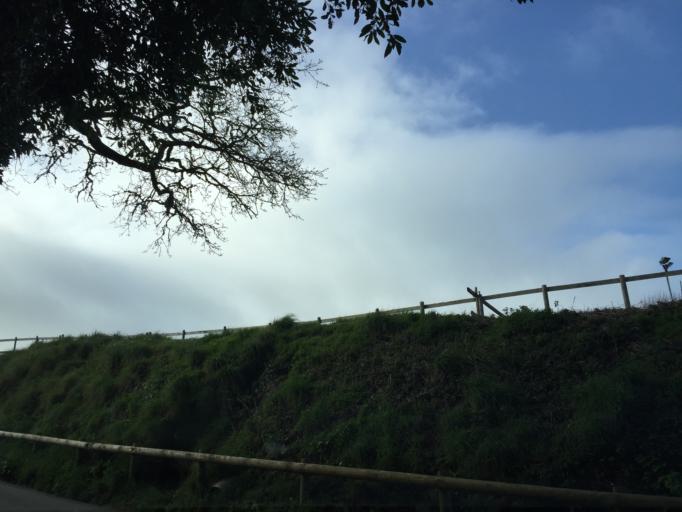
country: JE
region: St Helier
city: Saint Helier
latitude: 49.2109
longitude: -2.1551
